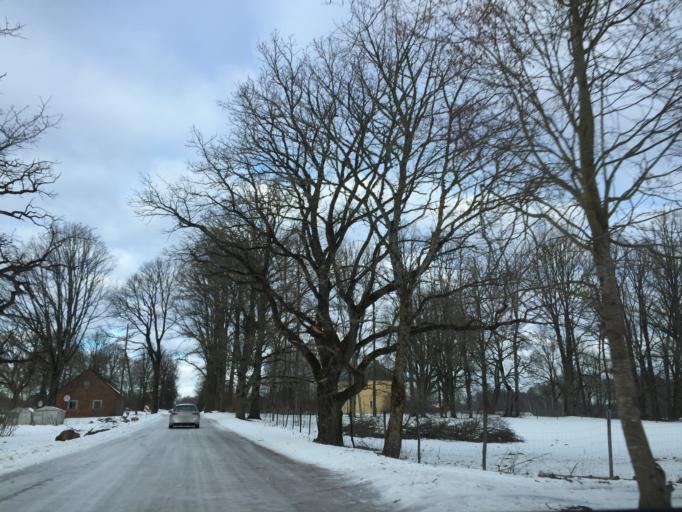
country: LV
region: Lielvarde
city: Lielvarde
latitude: 56.5642
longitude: 24.7343
